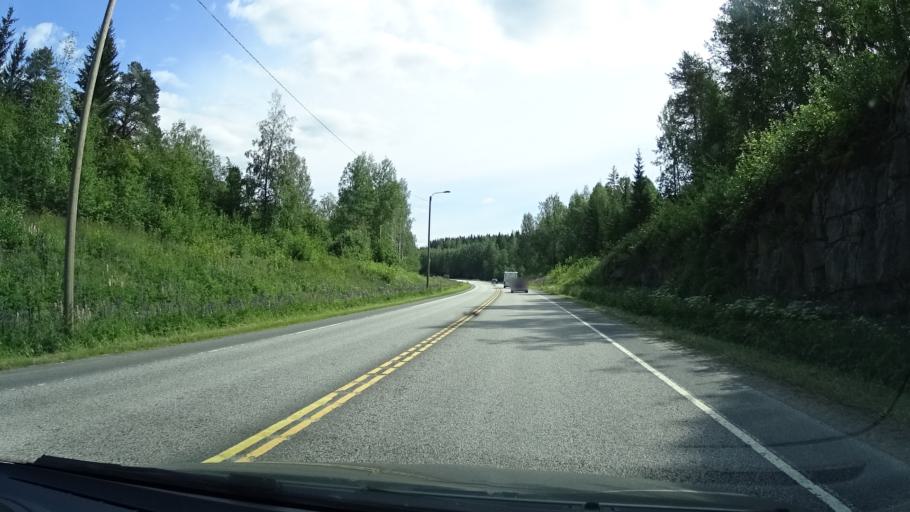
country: FI
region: Central Finland
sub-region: Jyvaeskylae
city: Jyvaeskylae
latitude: 62.2663
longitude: 25.5603
